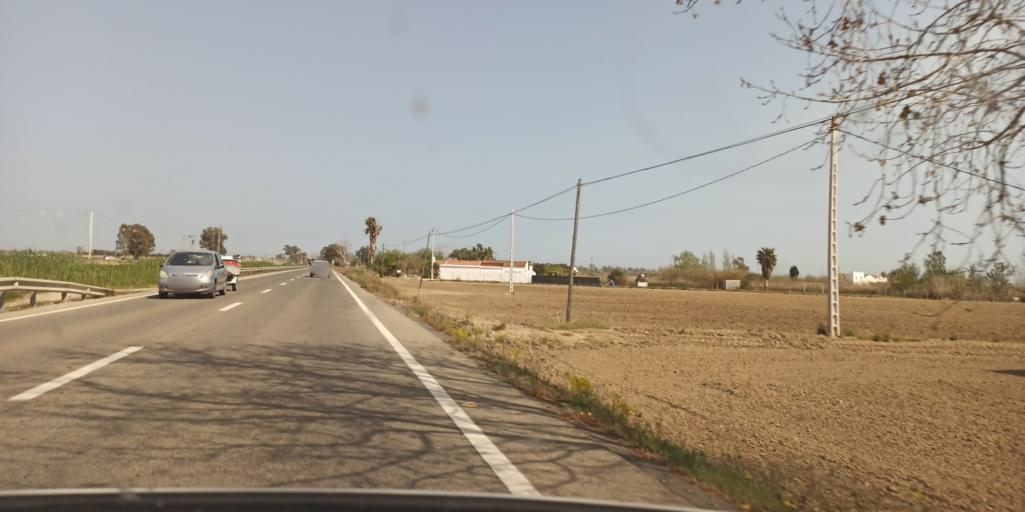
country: ES
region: Catalonia
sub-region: Provincia de Tarragona
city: Deltebre
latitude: 40.7060
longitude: 0.8038
